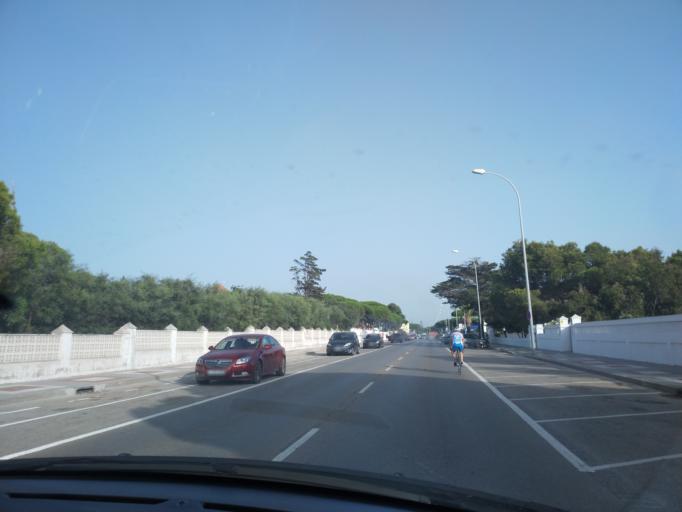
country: ES
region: Andalusia
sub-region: Provincia de Cadiz
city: Chiclana de la Frontera
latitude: 36.3737
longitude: -6.1837
